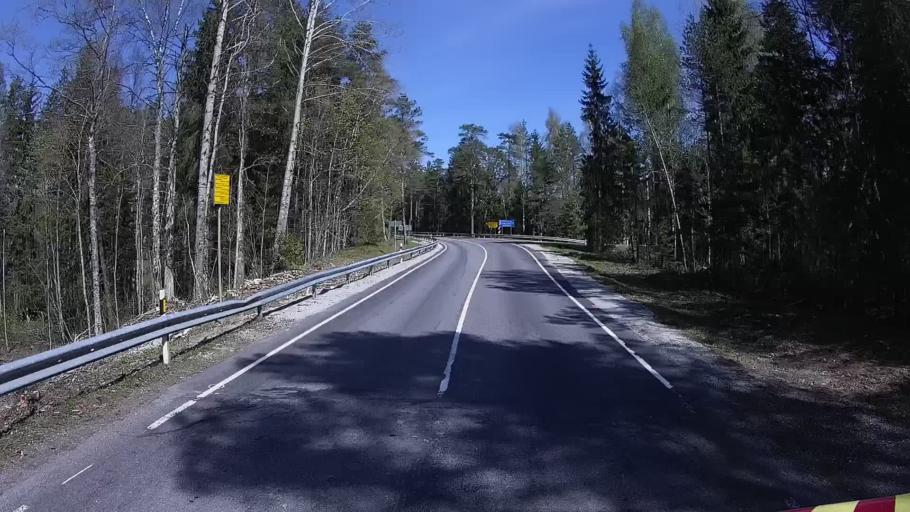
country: EE
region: Harju
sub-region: Nissi vald
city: Turba
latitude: 59.1298
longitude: 24.0708
